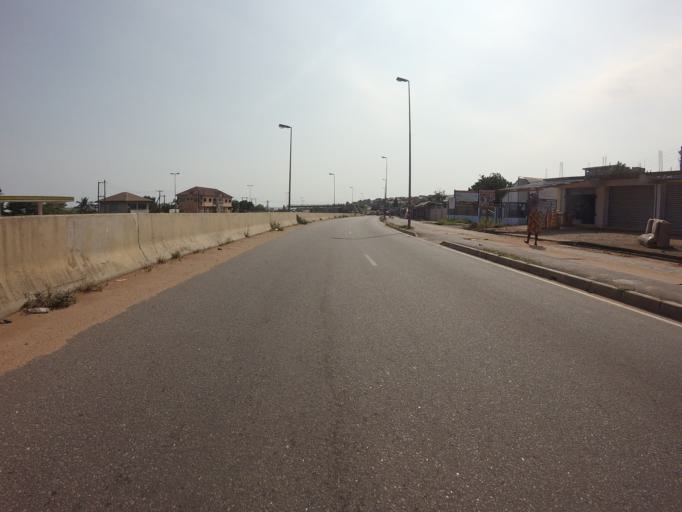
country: GH
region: Greater Accra
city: Gbawe
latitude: 5.6155
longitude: -0.2953
